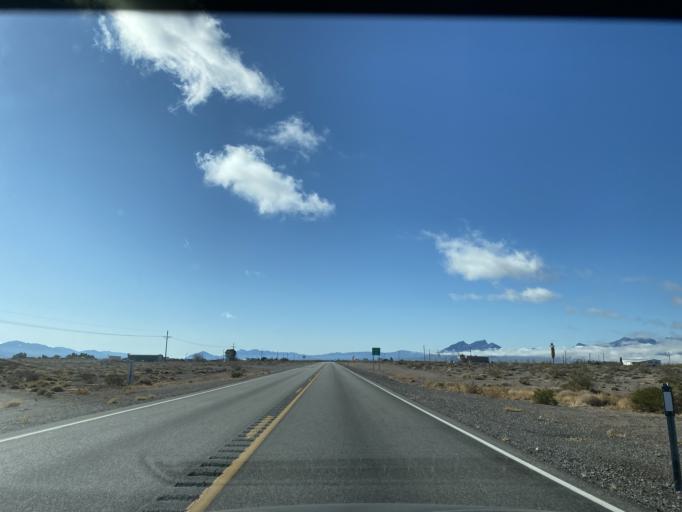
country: US
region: Nevada
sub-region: Nye County
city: Beatty
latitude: 36.5323
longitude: -116.4185
